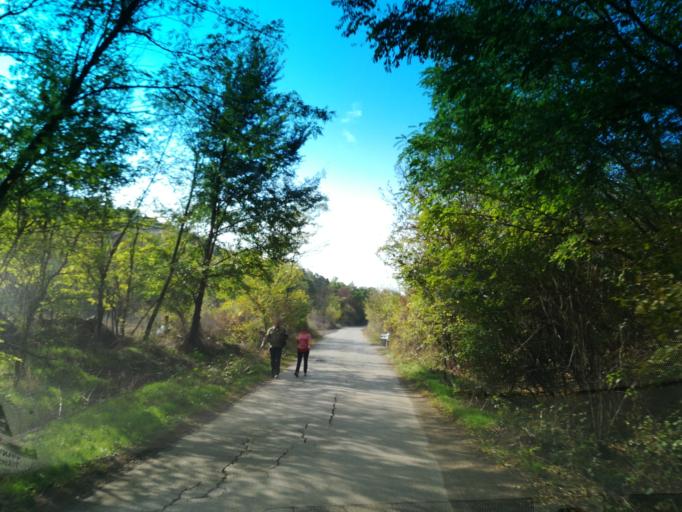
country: BG
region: Stara Zagora
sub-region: Obshtina Nikolaevo
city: Elkhovo
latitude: 42.3287
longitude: 25.4011
